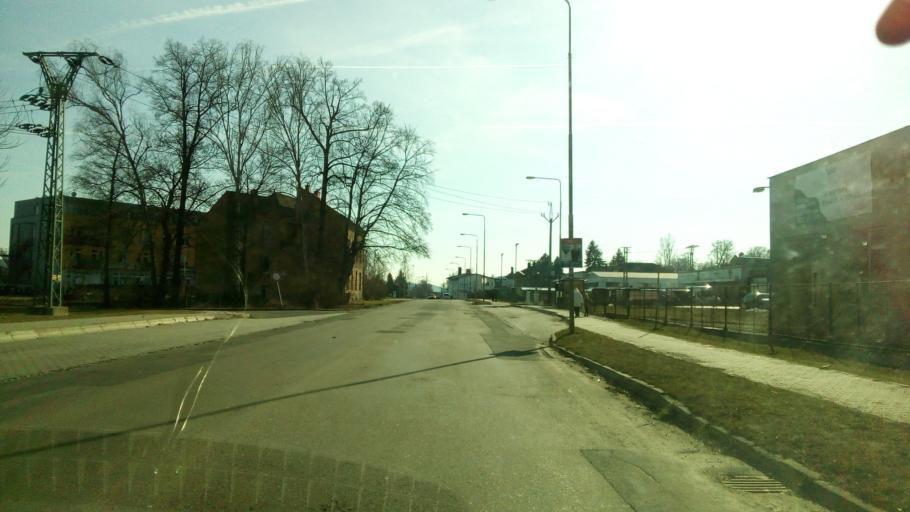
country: CZ
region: Olomoucky
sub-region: Okres Sumperk
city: Sumperk
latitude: 49.9579
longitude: 16.9624
